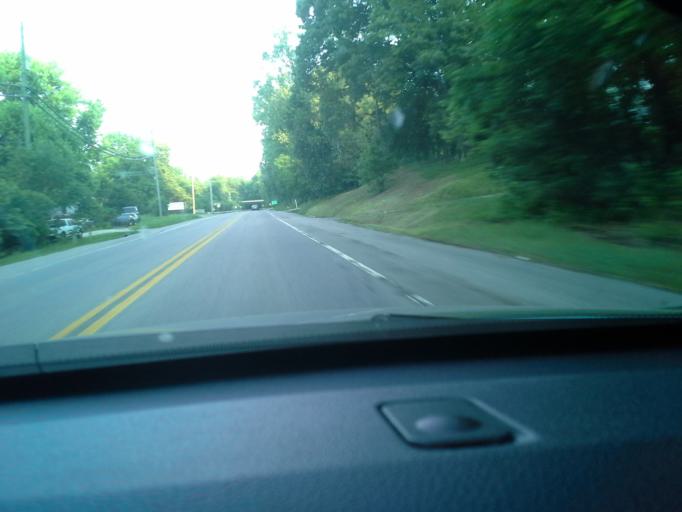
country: US
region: Maryland
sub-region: Calvert County
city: Owings
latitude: 38.7057
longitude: -76.5869
